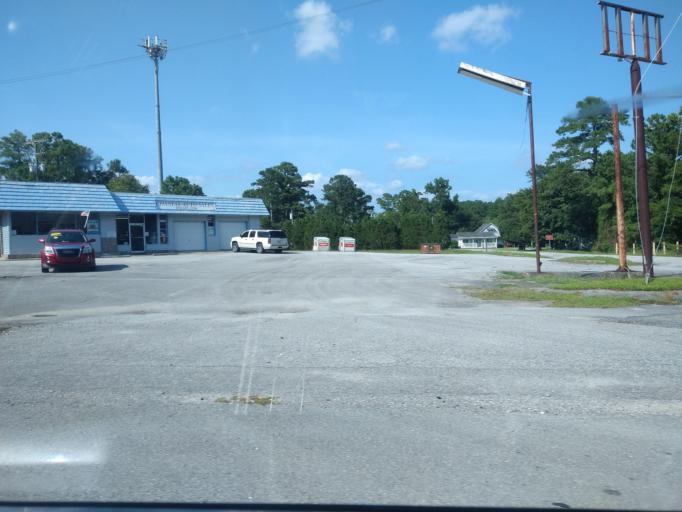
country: US
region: North Carolina
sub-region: Onslow County
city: Piney Green
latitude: 34.7378
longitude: -77.3580
